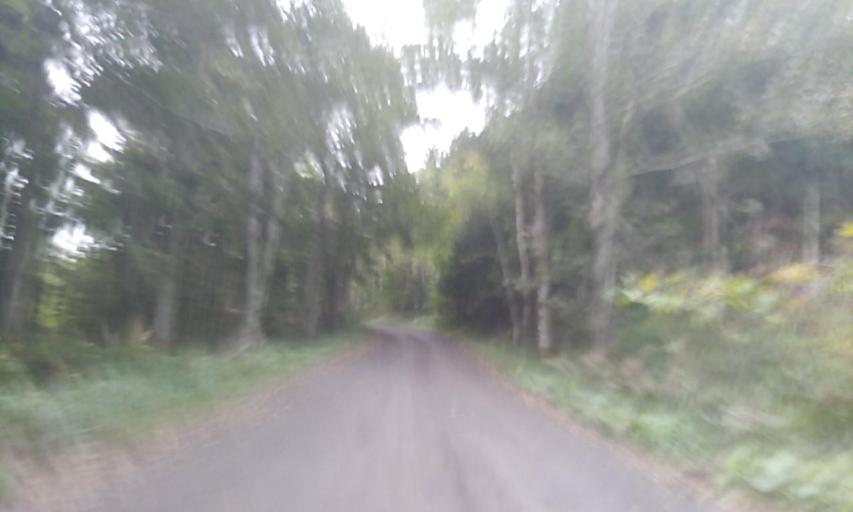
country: JP
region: Hokkaido
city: Abashiri
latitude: 43.6572
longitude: 144.5493
